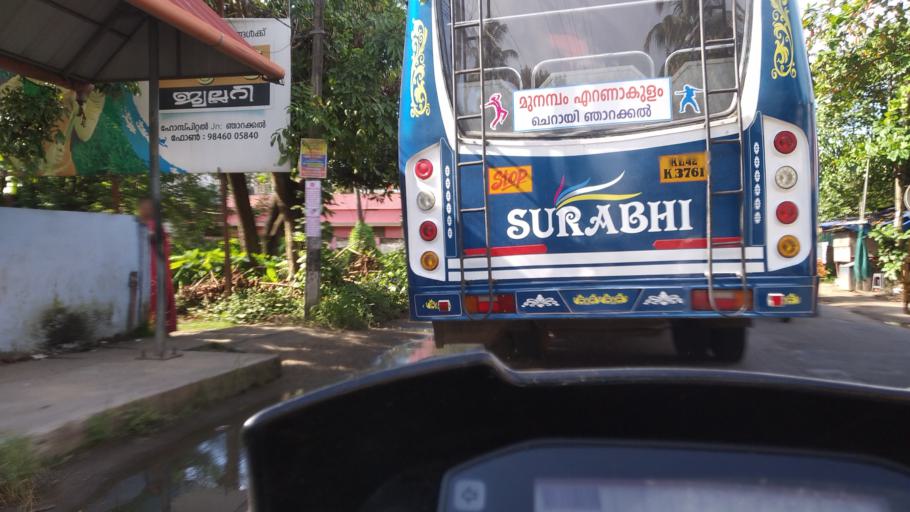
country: IN
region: Kerala
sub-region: Ernakulam
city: Elur
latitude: 10.0364
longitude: 76.2202
